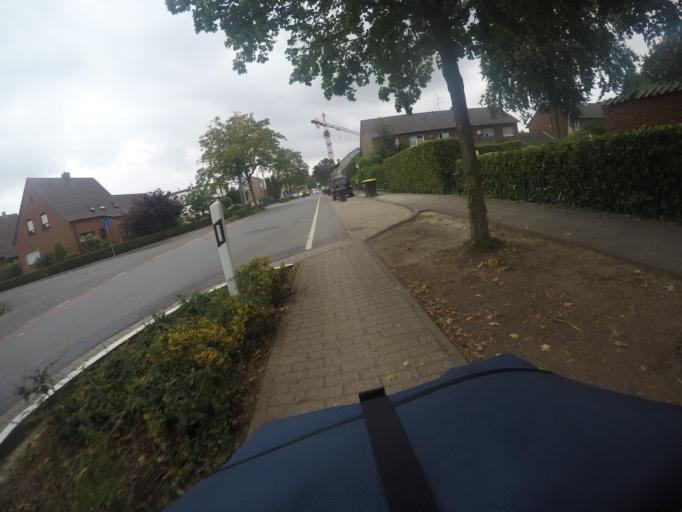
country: DE
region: North Rhine-Westphalia
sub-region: Regierungsbezirk Dusseldorf
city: Weeze
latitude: 51.6220
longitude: 6.2059
